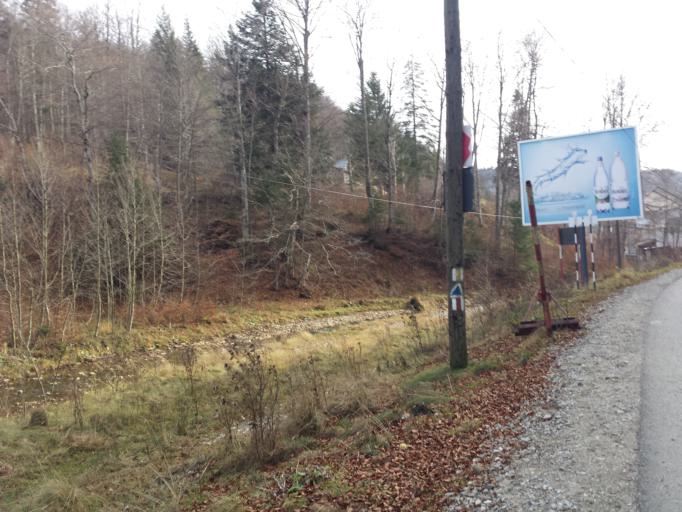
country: RO
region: Prahova
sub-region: Oras Azuga
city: Azuga
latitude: 45.4265
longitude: 25.5375
